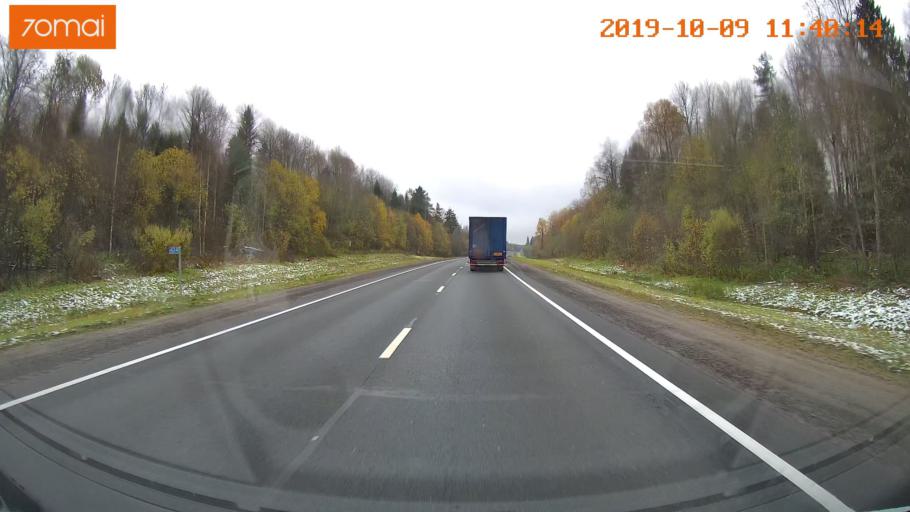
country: RU
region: Vologda
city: Gryazovets
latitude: 58.9453
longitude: 40.1732
